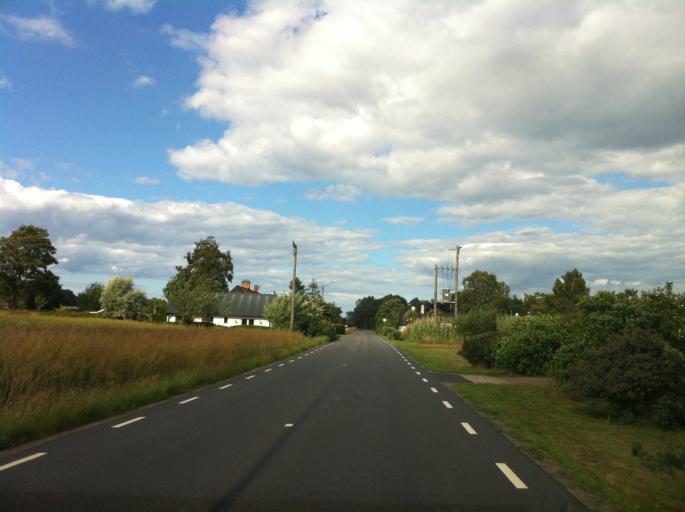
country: SE
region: Skane
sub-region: Simrishamns Kommun
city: Simrishamn
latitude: 55.4405
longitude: 14.2365
